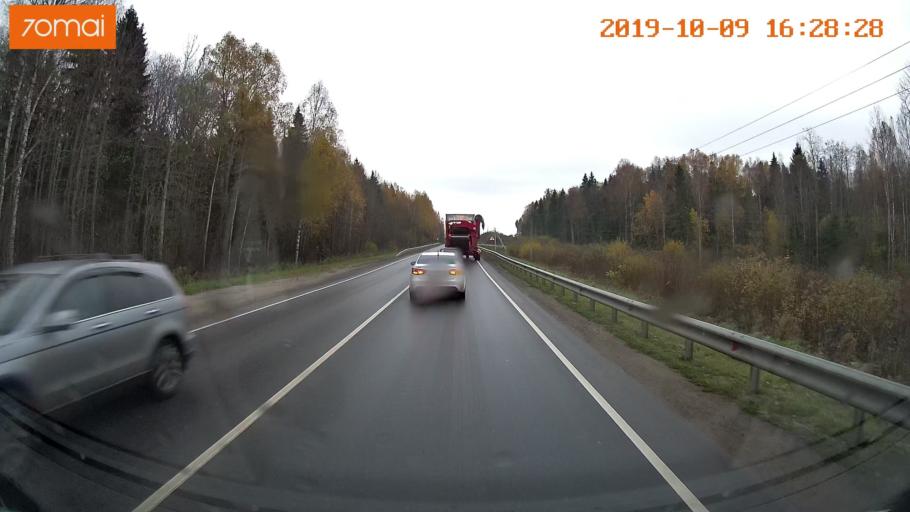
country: RU
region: Kostroma
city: Oktyabr'skiy
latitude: 57.6286
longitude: 40.9321
